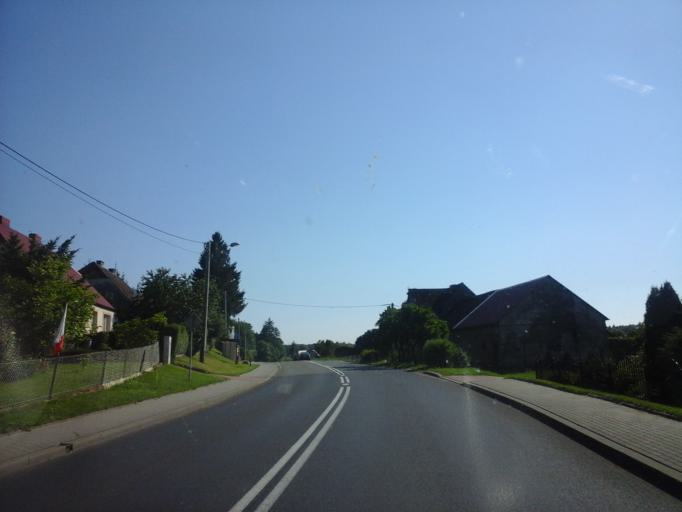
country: PL
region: West Pomeranian Voivodeship
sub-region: Powiat gryficki
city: Brojce
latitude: 53.9039
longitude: 15.4293
